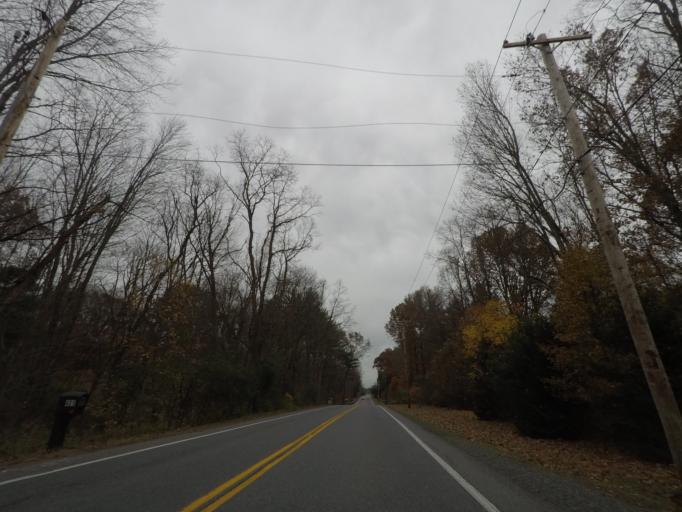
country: US
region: New York
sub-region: Saratoga County
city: Country Knolls
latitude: 42.8556
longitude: -73.8202
